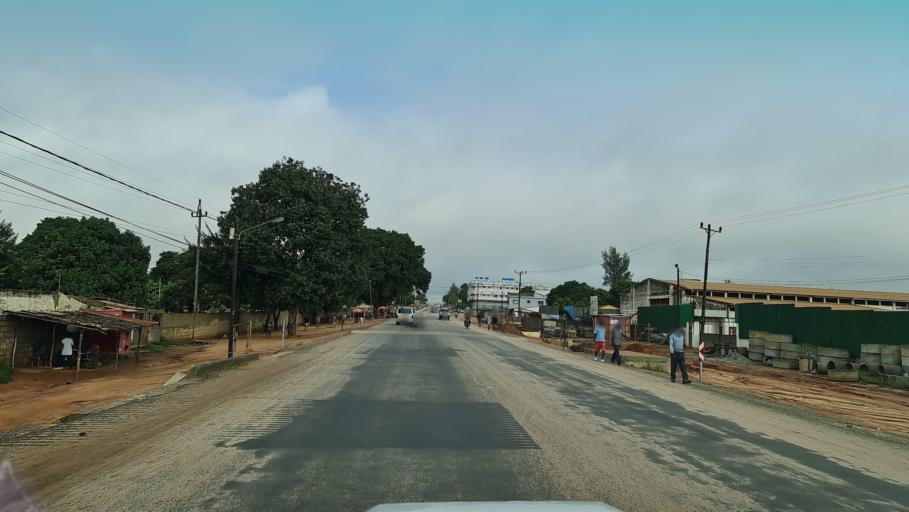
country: MZ
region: Nampula
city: Nampula
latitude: -15.1391
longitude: 39.2874
